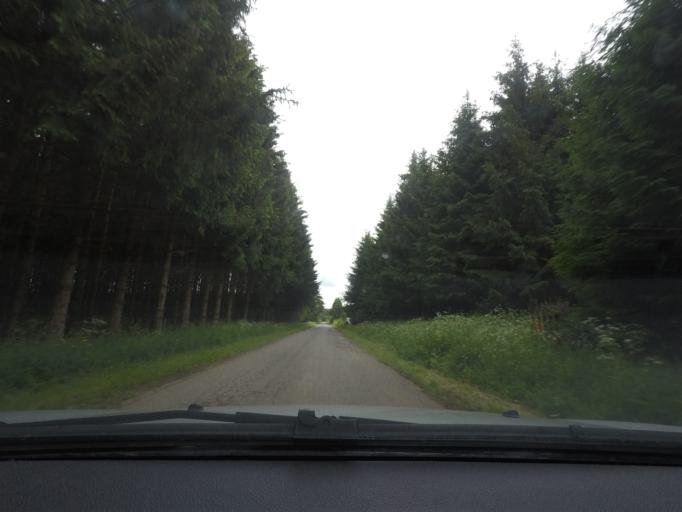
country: BE
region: Wallonia
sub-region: Province du Luxembourg
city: Leglise
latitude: 49.8218
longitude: 5.5196
